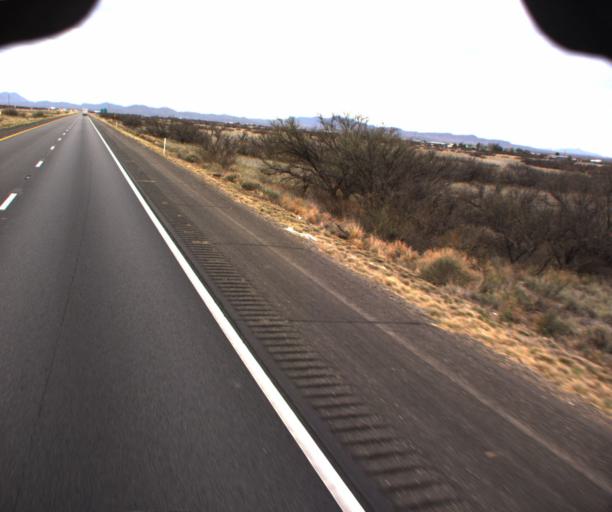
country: US
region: Arizona
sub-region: Cochise County
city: Willcox
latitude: 32.2446
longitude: -109.8611
